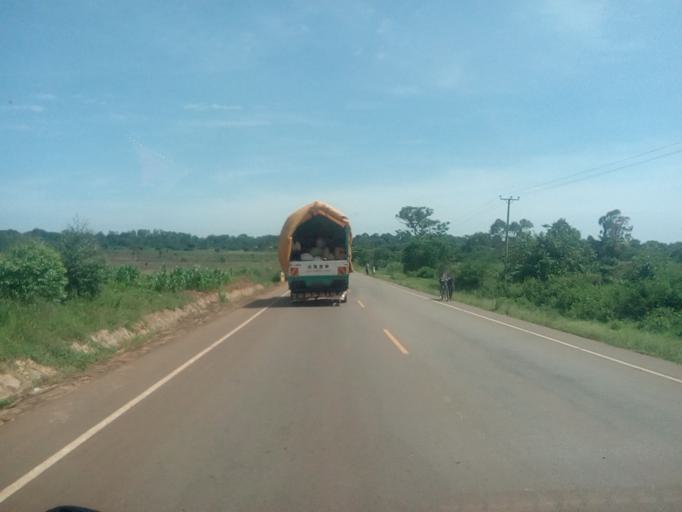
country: UG
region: Eastern Region
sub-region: Jinja District
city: Buwenge
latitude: 0.7301
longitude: 33.1537
